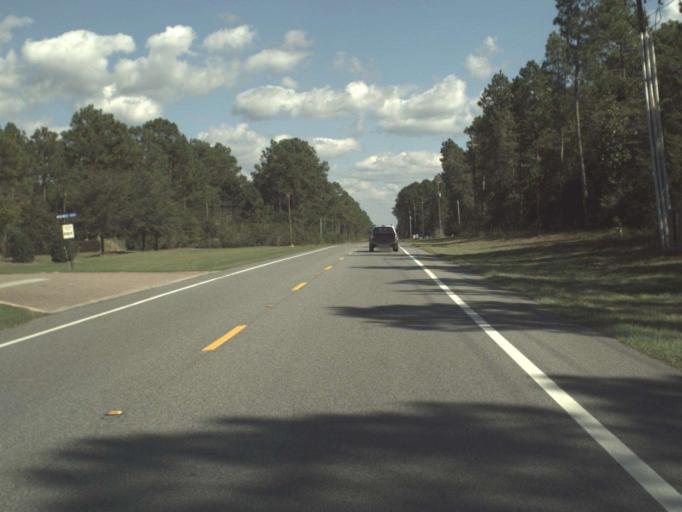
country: US
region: Florida
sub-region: Walton County
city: Freeport
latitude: 30.4766
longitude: -86.0325
